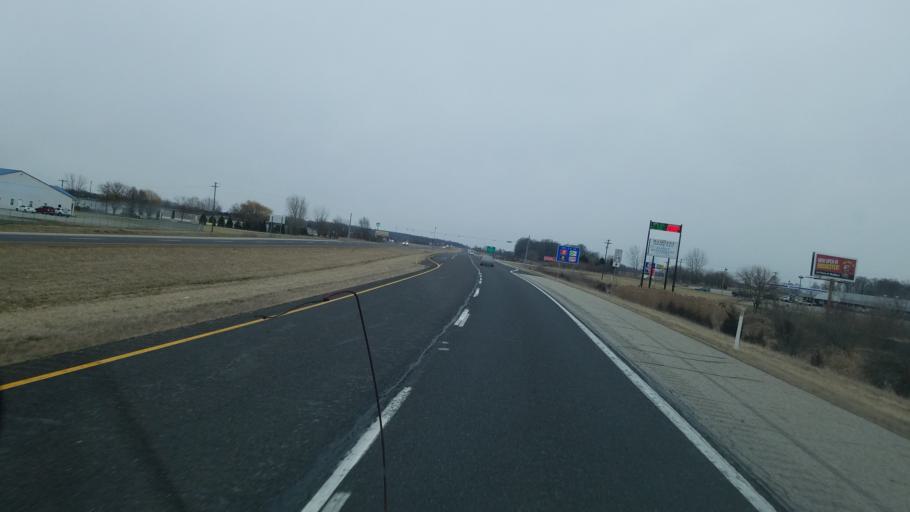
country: US
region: Indiana
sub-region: Fulton County
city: Rochester
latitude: 41.0491
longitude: -86.2338
